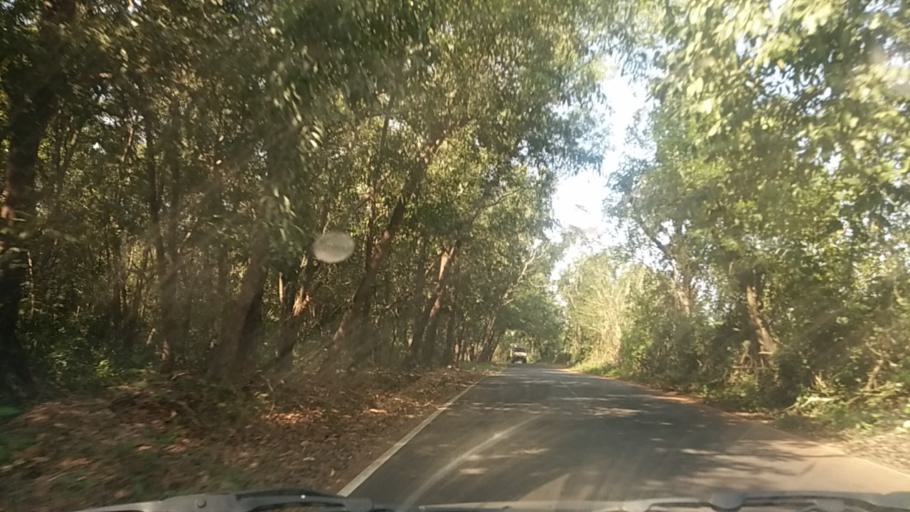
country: IN
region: Goa
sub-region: South Goa
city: Sanguem
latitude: 15.2130
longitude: 74.2116
